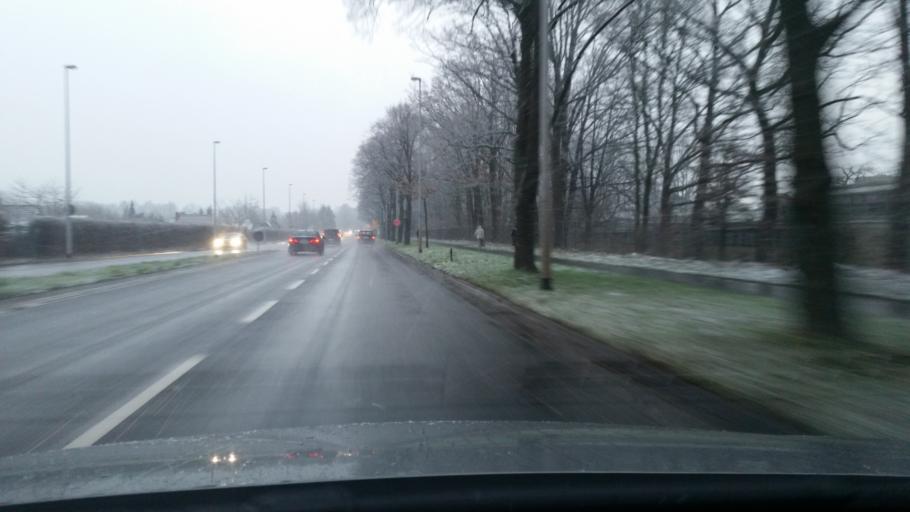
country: DE
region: Lower Saxony
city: Hemmingen
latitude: 52.3432
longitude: 9.6979
